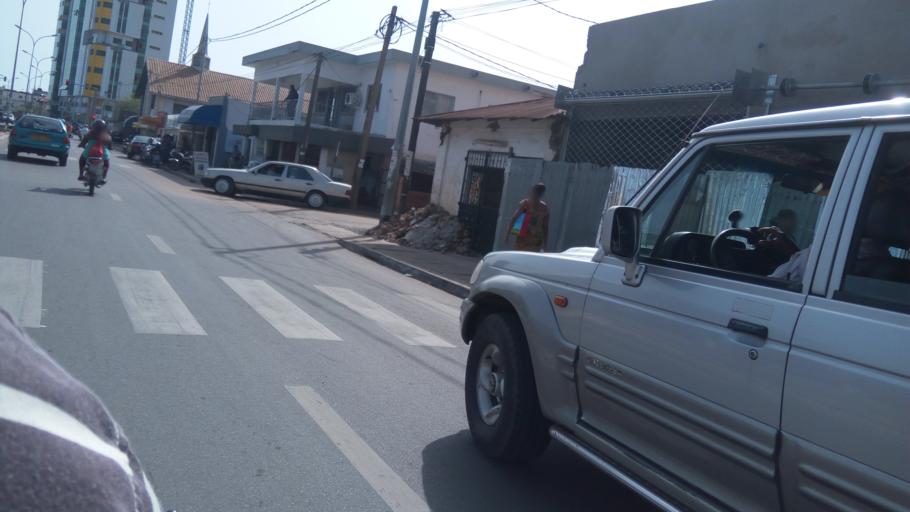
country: TG
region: Maritime
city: Lome
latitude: 6.1345
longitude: 1.2166
